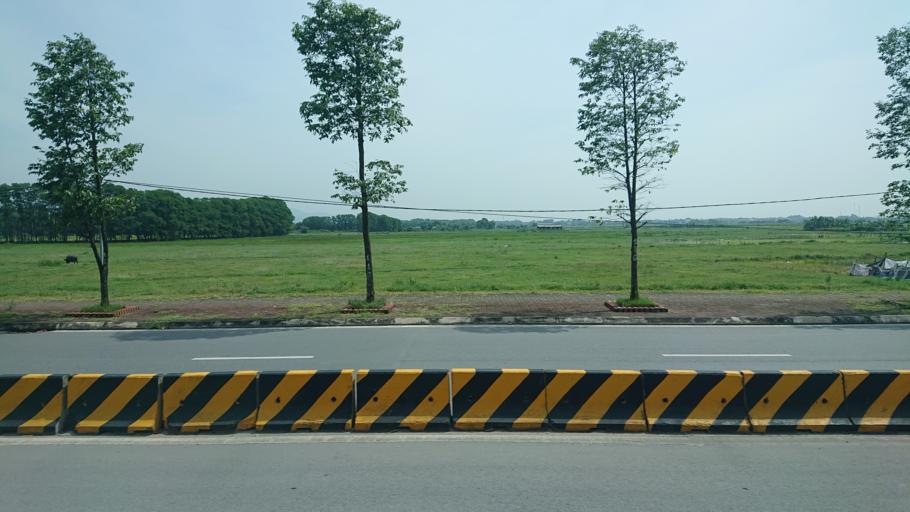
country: VN
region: Ha Noi
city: Soc Son
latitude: 21.2068
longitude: 105.8249
